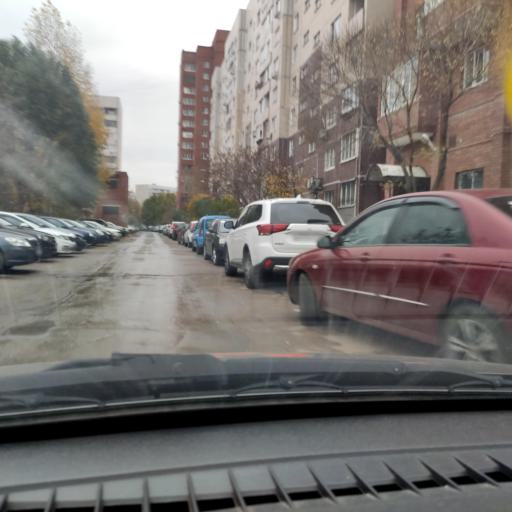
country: RU
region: Samara
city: Tol'yatti
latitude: 53.5473
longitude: 49.3222
